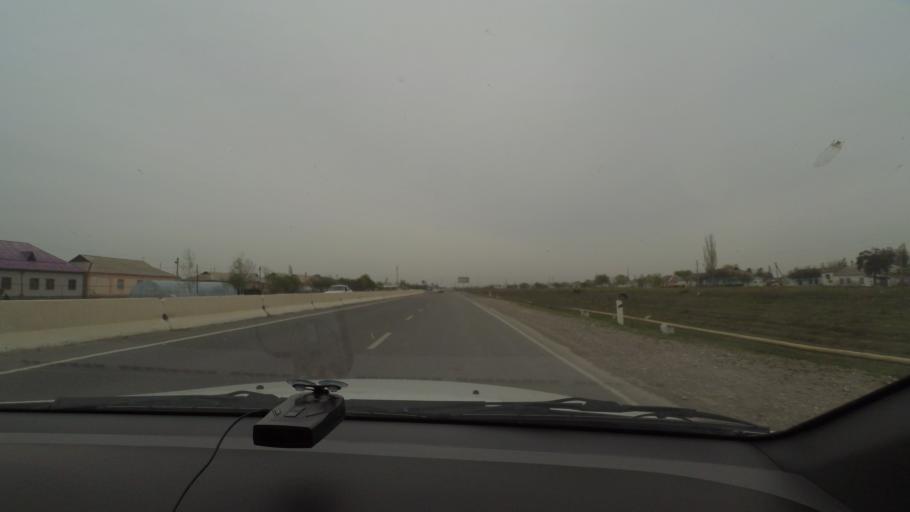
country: UZ
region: Sirdaryo
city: Guliston
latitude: 40.4918
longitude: 68.6958
